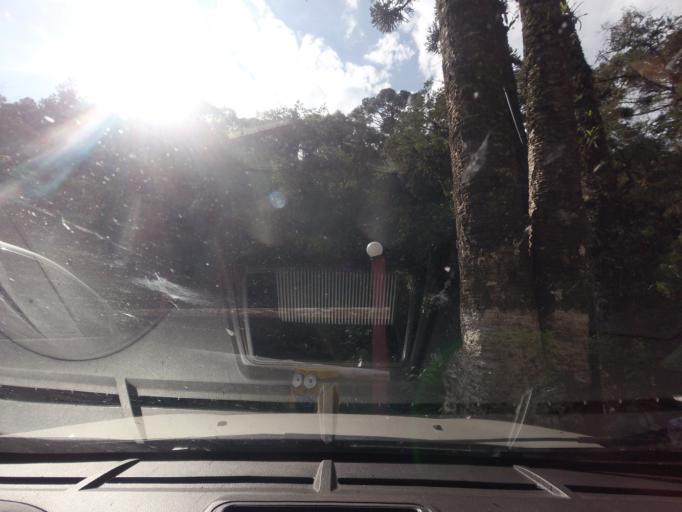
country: BR
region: Sao Paulo
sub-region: Campos Do Jordao
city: Campos do Jordao
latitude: -22.7182
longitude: -45.5558
